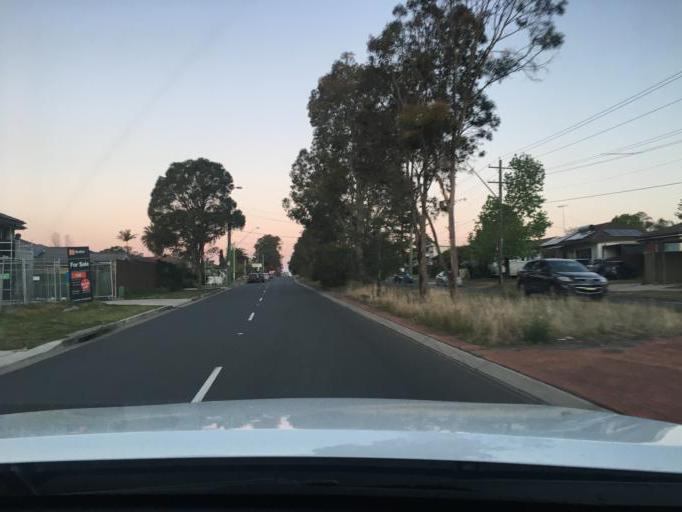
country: AU
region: New South Wales
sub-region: Fairfield
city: Fairfield Heights
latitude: -33.8481
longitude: 150.9186
